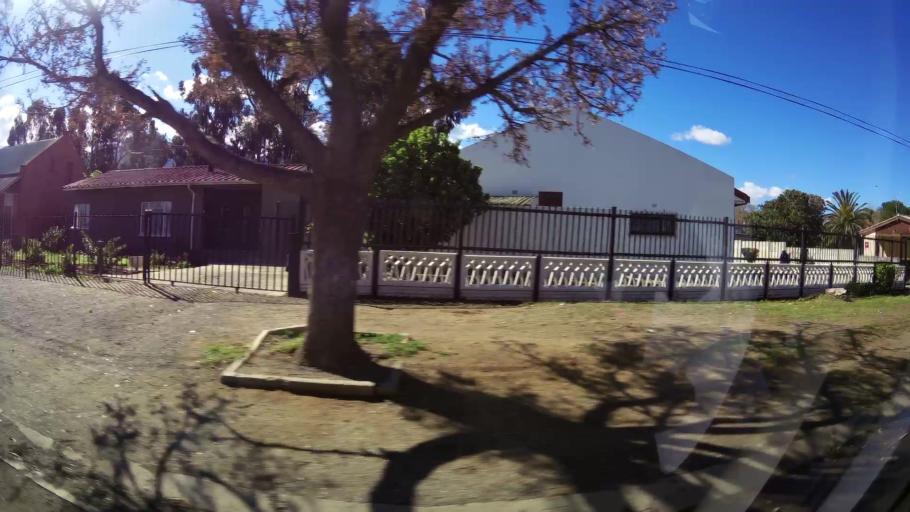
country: ZA
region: Western Cape
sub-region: Cape Winelands District Municipality
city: Ashton
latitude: -33.7879
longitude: 19.8881
